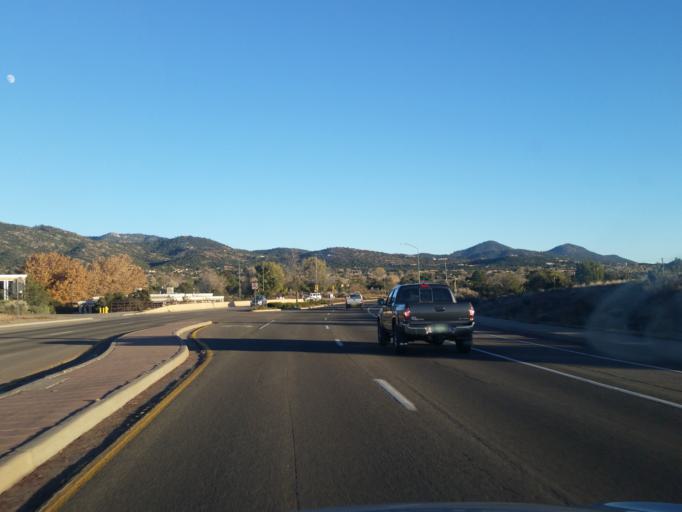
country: US
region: New Mexico
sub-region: Santa Fe County
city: Santa Fe
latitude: 35.6556
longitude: -105.9409
